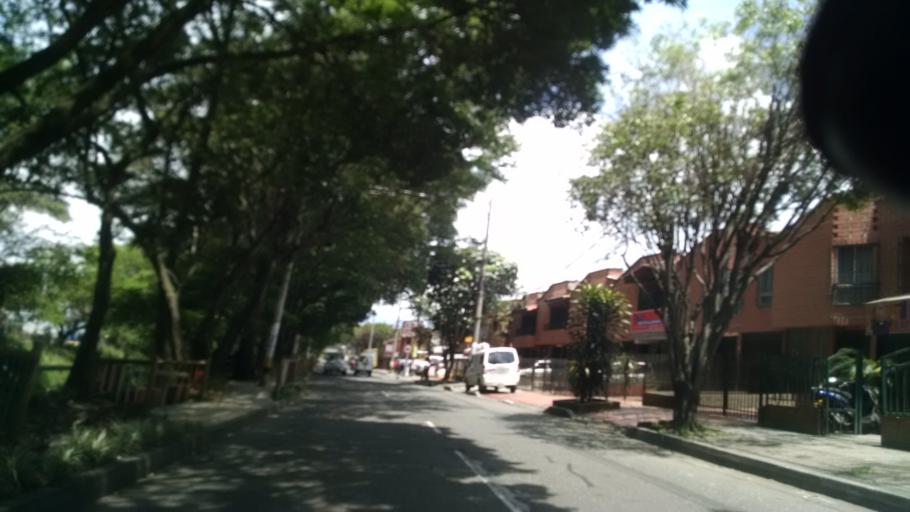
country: CO
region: Antioquia
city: Medellin
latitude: 6.2202
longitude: -75.5849
